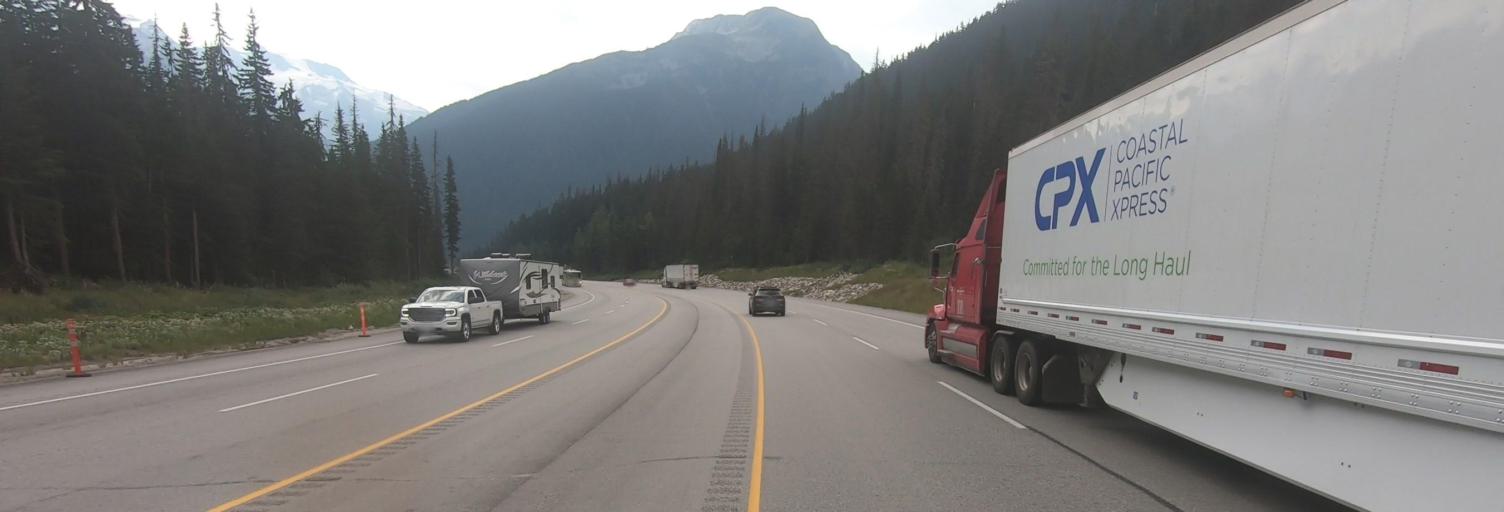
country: CA
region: British Columbia
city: Golden
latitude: 51.2835
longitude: -117.5137
